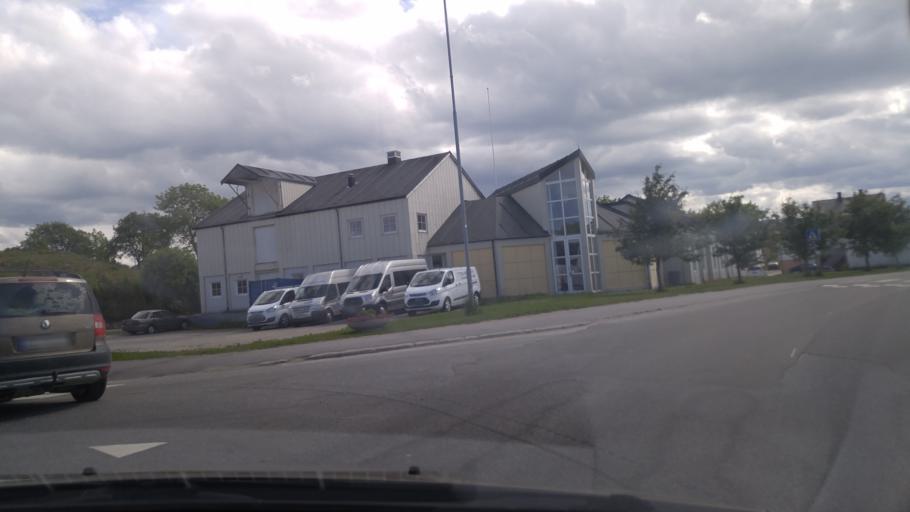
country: NO
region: Nord-Trondelag
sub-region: Vikna
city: Rorvik
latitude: 64.8621
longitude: 11.2318
